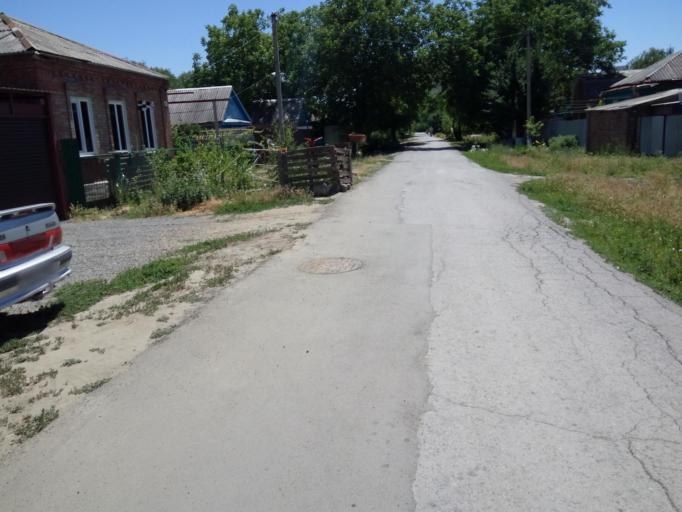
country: RU
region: Rostov
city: Bataysk
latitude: 47.1416
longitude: 39.7710
